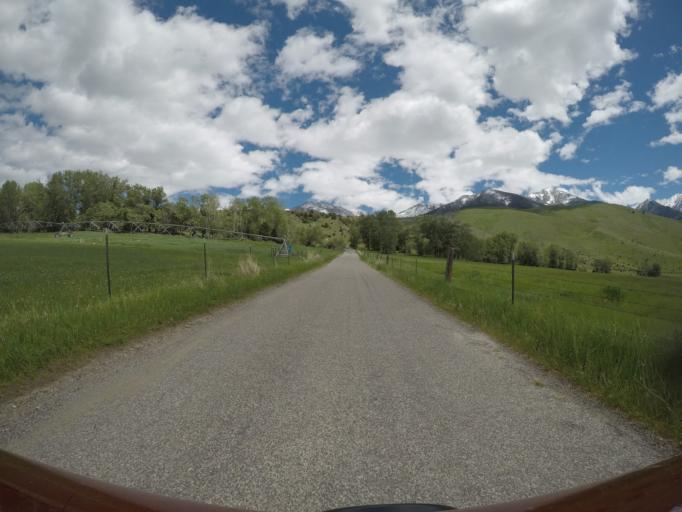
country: US
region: Montana
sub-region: Park County
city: Livingston
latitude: 45.4967
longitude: -110.5622
